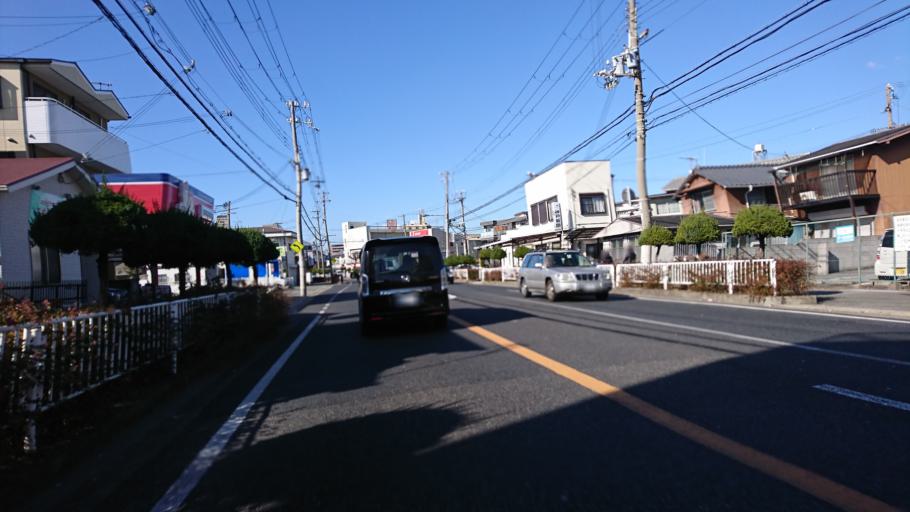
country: JP
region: Hyogo
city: Akashi
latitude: 34.6482
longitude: 134.9804
